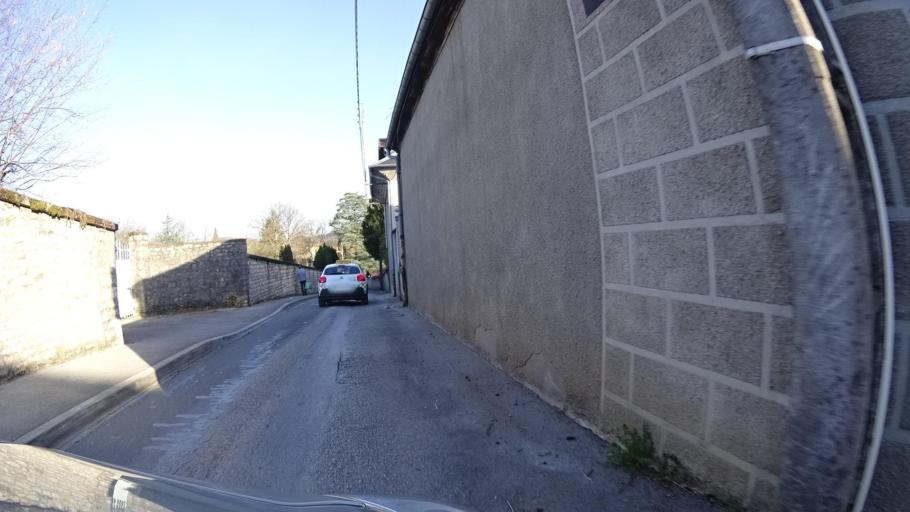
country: FR
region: Franche-Comte
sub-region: Departement du Doubs
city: Beure
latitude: 47.2312
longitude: 5.9885
